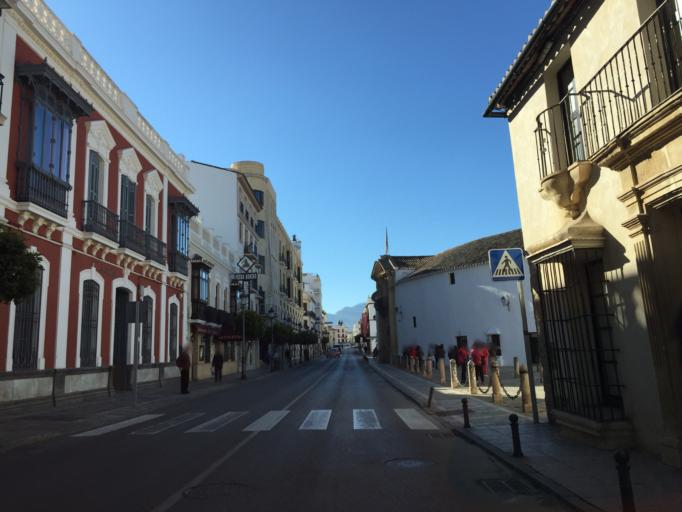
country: ES
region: Andalusia
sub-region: Provincia de Malaga
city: Ronda
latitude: 36.7431
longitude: -5.1669
